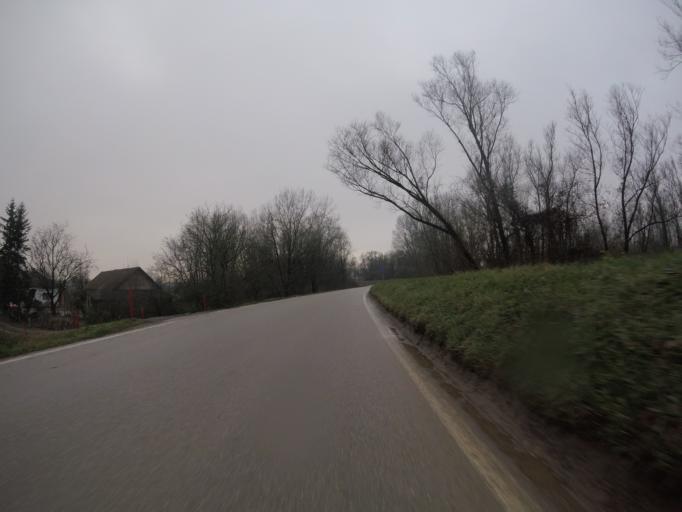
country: HR
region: Zagrebacka
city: Kuce
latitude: 45.6978
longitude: 16.2156
